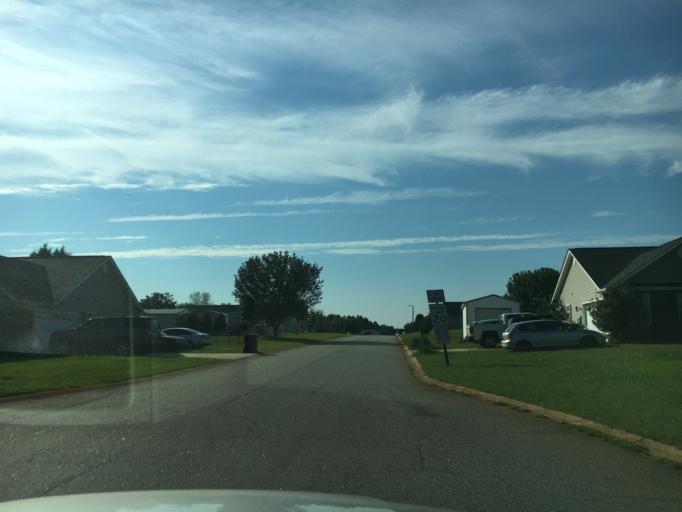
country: US
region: South Carolina
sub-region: Spartanburg County
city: Boiling Springs
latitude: 35.0855
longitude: -81.9354
